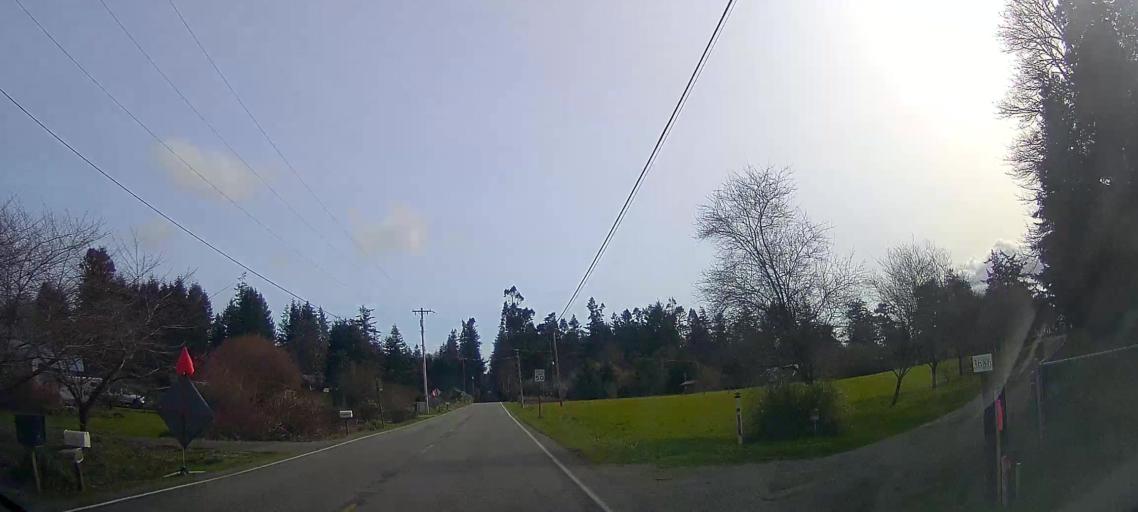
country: US
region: Washington
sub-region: Island County
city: Langley
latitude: 48.0926
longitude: -122.4086
